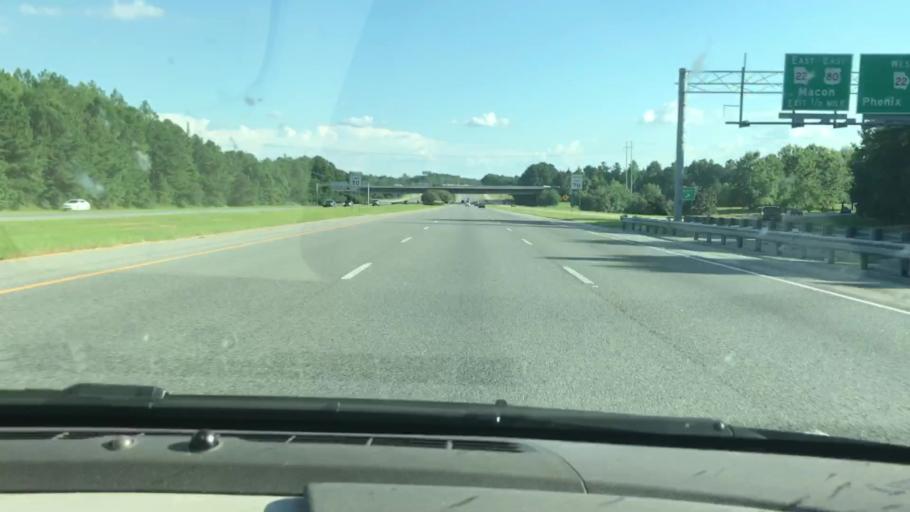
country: US
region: Alabama
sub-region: Russell County
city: Phenix City
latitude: 32.5494
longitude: -84.9619
